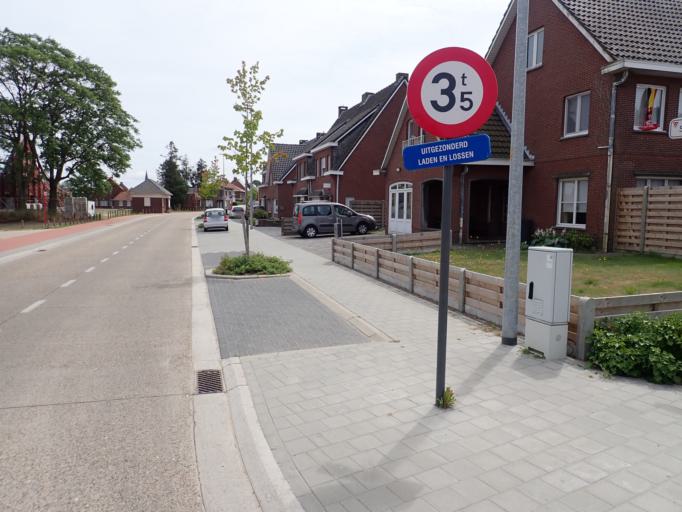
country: BE
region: Flanders
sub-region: Provincie Antwerpen
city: Rijkevorsel
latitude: 51.3300
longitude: 4.7736
